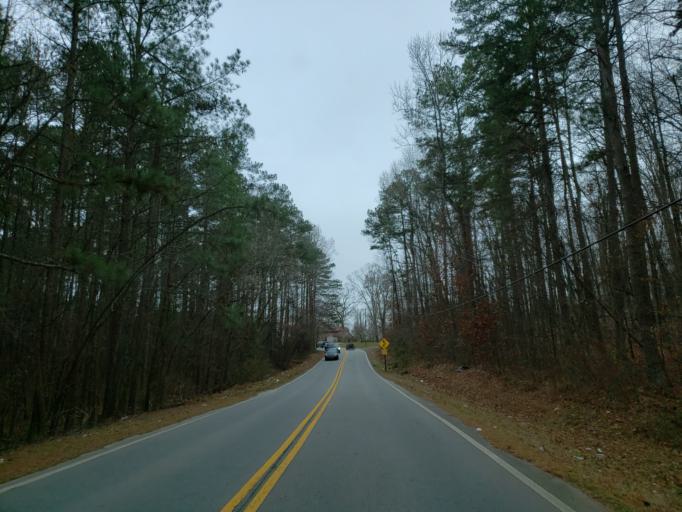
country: US
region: Georgia
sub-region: Paulding County
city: Hiram
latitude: 33.9191
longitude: -84.7231
